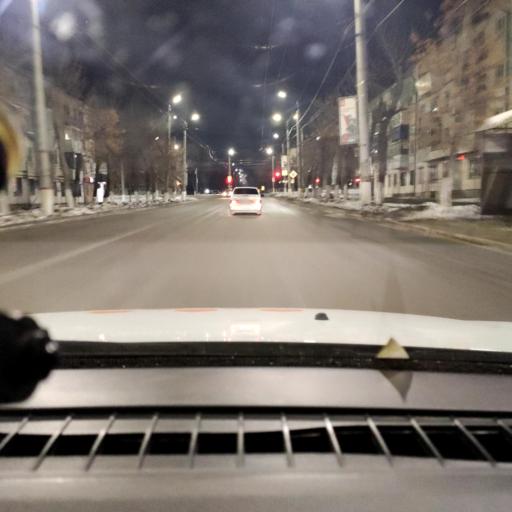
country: RU
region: Samara
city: Novokuybyshevsk
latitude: 53.0874
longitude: 49.9506
